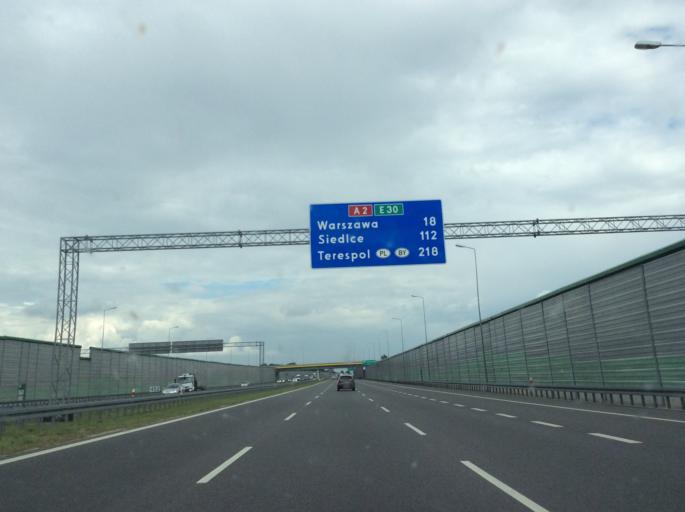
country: PL
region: Masovian Voivodeship
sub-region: Powiat warszawski zachodni
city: Ozarow Mazowiecki
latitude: 52.1907
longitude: 20.7921
